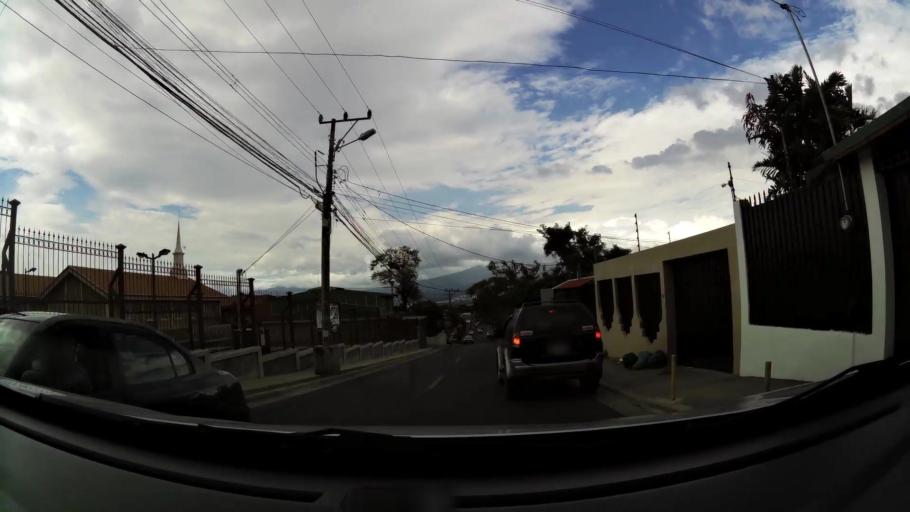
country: CR
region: San Jose
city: Escazu
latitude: 9.9191
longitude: -84.1434
